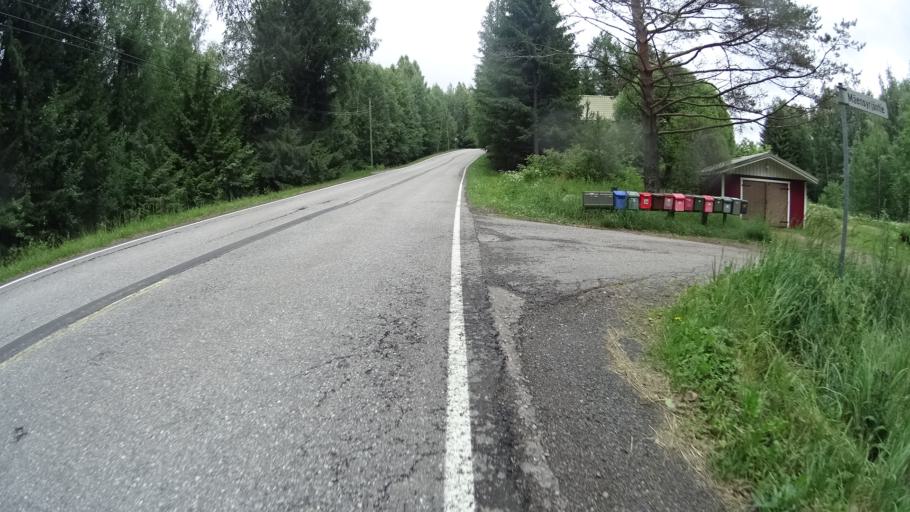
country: FI
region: Uusimaa
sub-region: Helsinki
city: Karkkila
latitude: 60.5762
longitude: 24.3259
